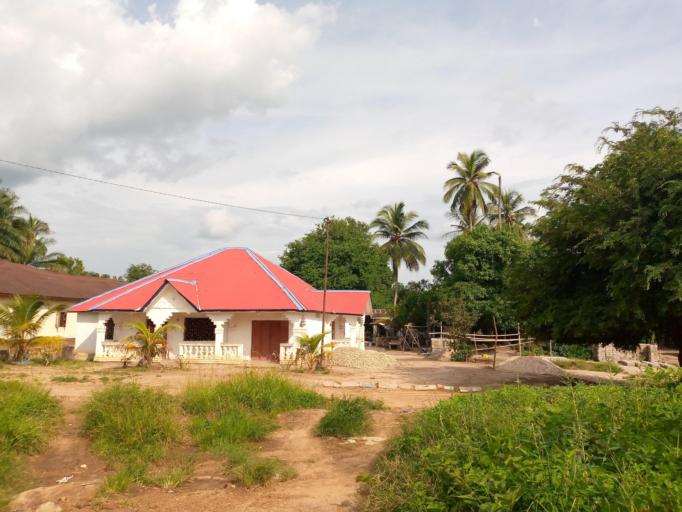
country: SL
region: Northern Province
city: Magburaka
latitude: 8.7194
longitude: -11.9555
